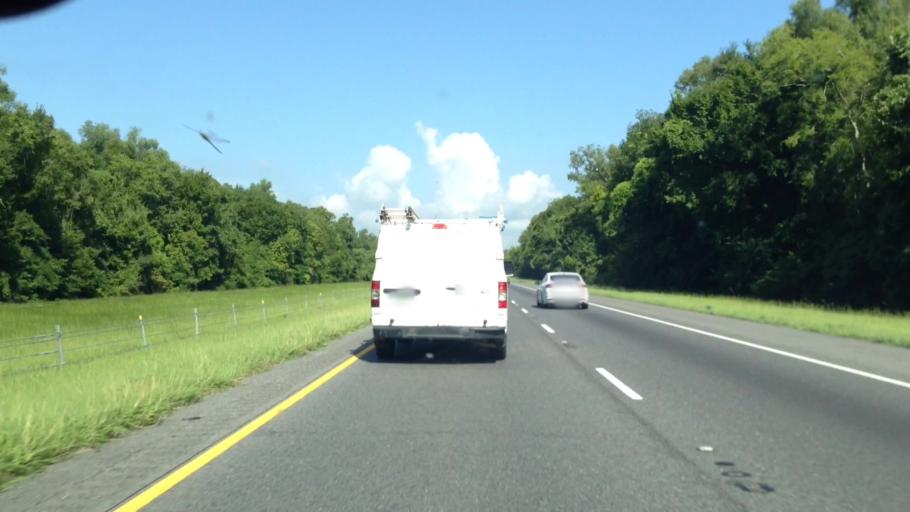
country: US
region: Louisiana
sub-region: Ascension Parish
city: Sorrento
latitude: 30.1627
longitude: -90.8443
